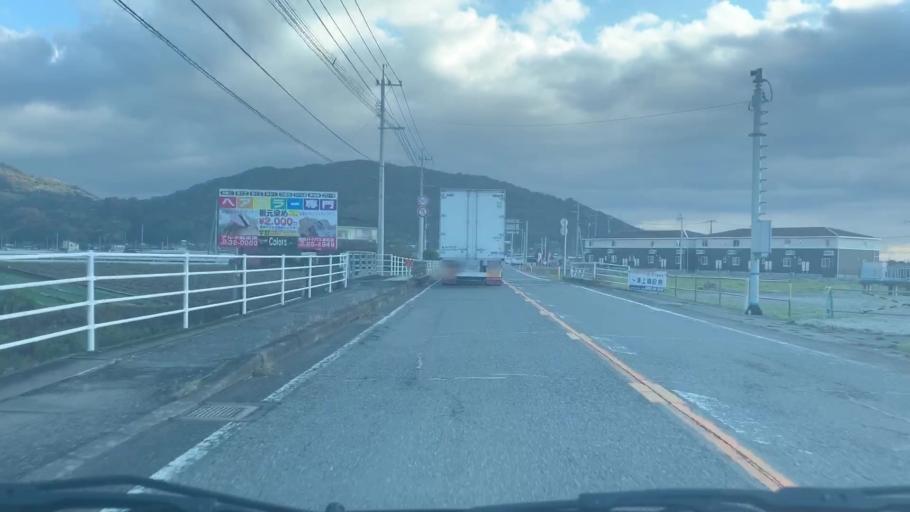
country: JP
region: Saga Prefecture
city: Kashima
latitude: 33.2191
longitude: 130.1431
